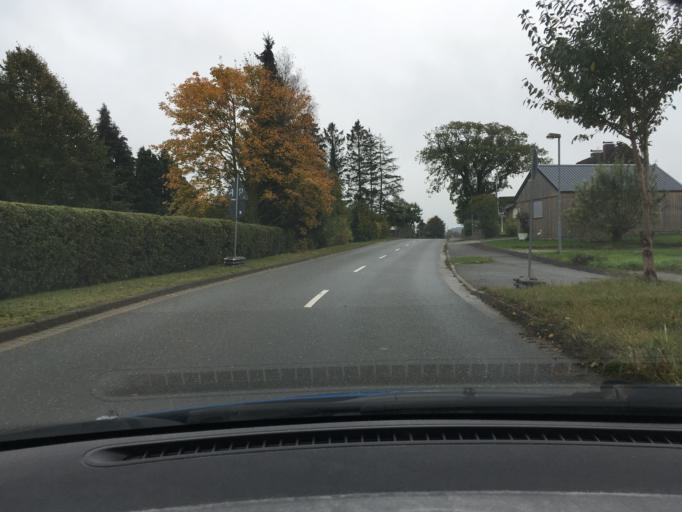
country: DE
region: Schleswig-Holstein
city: Bosdorf
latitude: 54.1232
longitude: 10.4754
